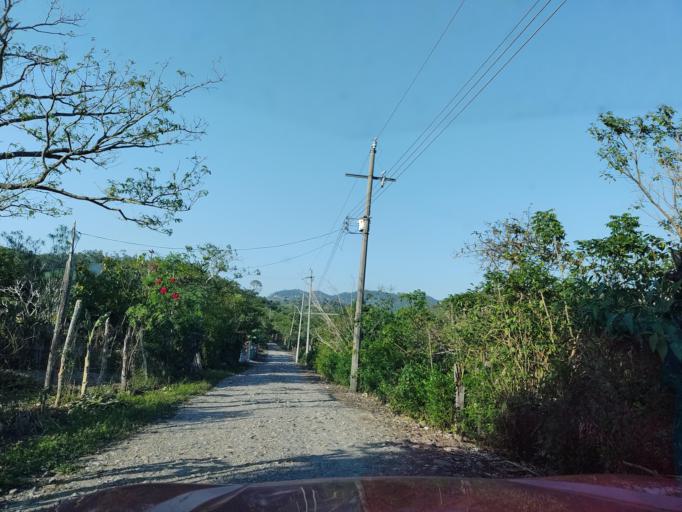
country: MX
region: Veracruz
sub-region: Papantla
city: Polutla
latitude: 20.4482
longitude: -97.2430
